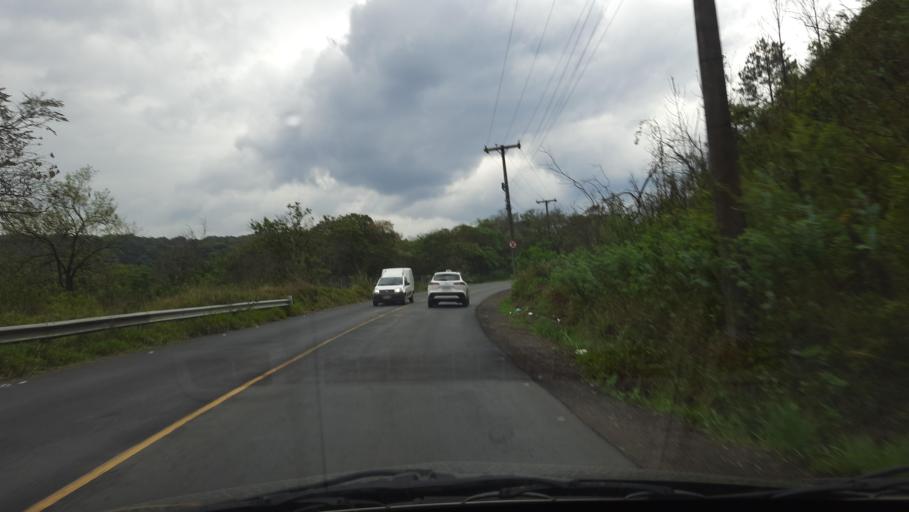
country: BR
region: Sao Paulo
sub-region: Caieiras
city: Caieiras
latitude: -23.3658
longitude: -46.6687
